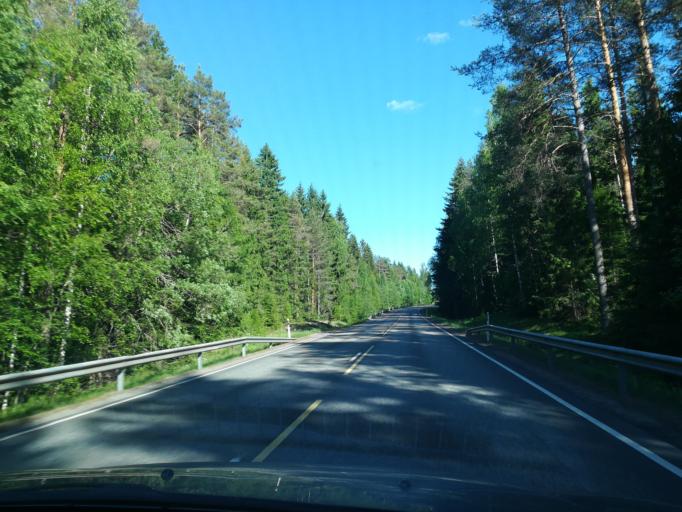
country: FI
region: South Karelia
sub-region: Imatra
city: Ruokolahti
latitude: 61.3571
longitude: 28.7141
